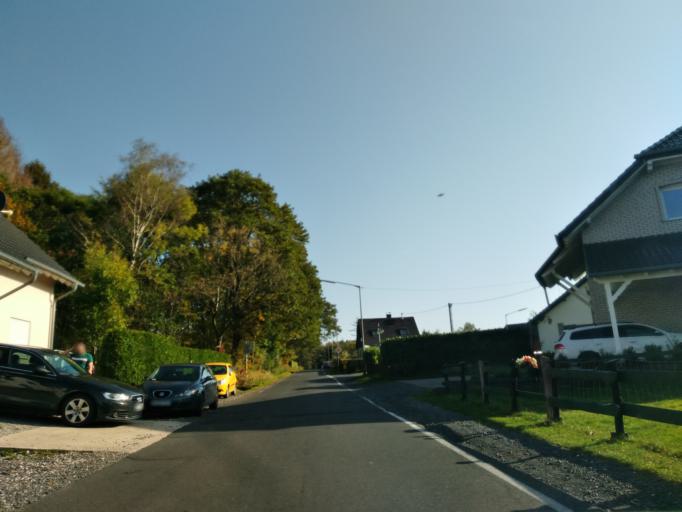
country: DE
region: Rheinland-Pfalz
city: Kircheib
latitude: 50.7082
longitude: 7.4683
